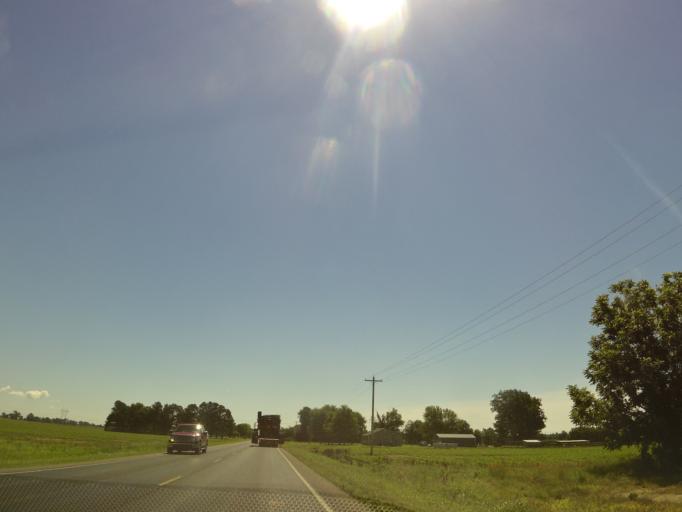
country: US
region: Missouri
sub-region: New Madrid County
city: Portageville
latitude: 36.5539
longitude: -89.7627
